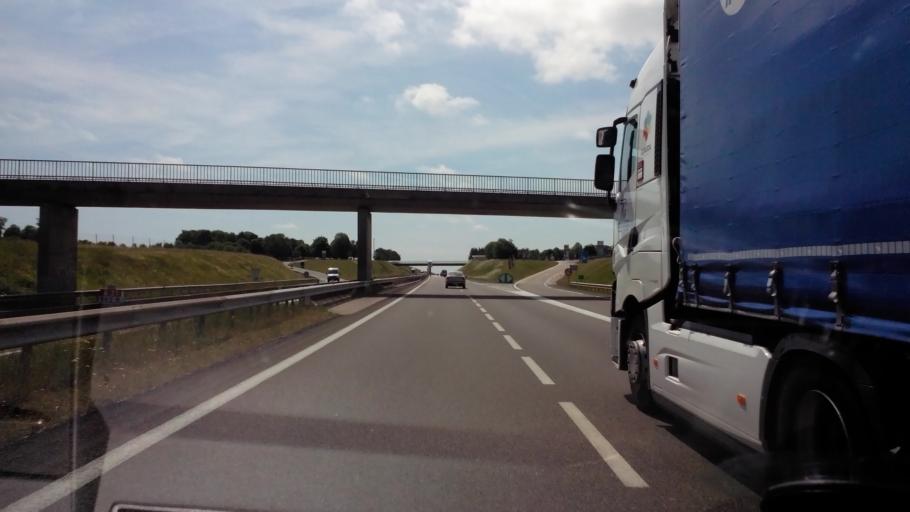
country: FR
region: Lorraine
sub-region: Departement des Vosges
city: Chatenois
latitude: 48.2725
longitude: 5.8591
